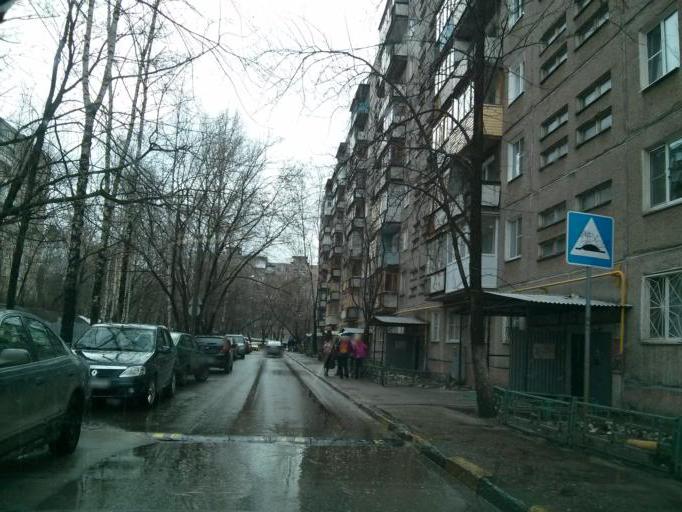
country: RU
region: Nizjnij Novgorod
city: Nizhniy Novgorod
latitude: 56.3170
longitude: 44.0467
